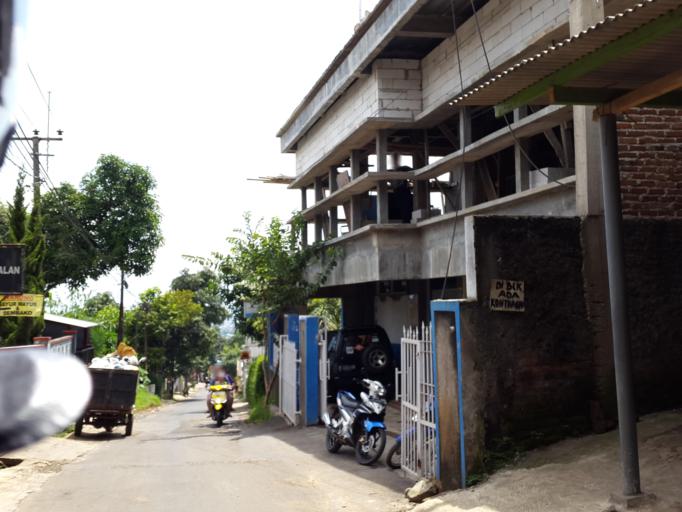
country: ID
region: West Java
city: Bandung
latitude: -6.8889
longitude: 107.6661
